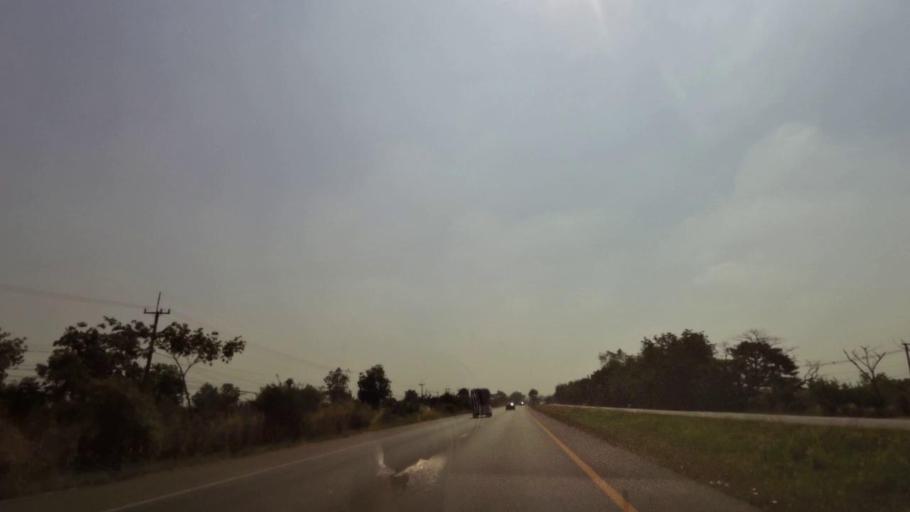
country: TH
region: Phichit
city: Wachira Barami
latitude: 16.4765
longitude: 100.1471
